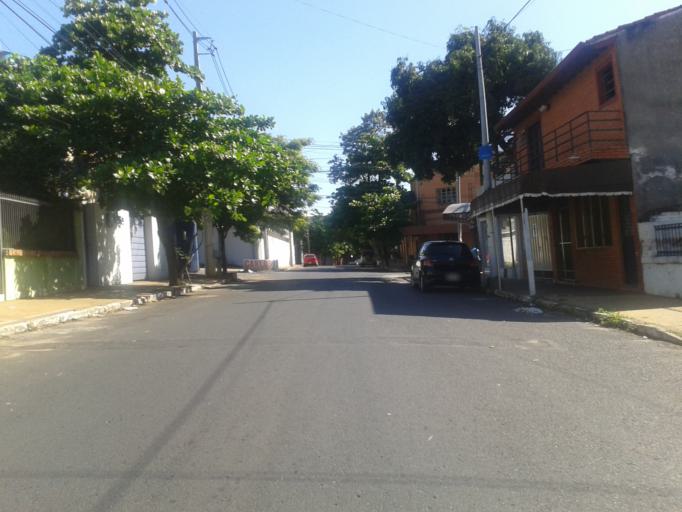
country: PY
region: Asuncion
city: Asuncion
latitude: -25.2934
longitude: -57.6374
